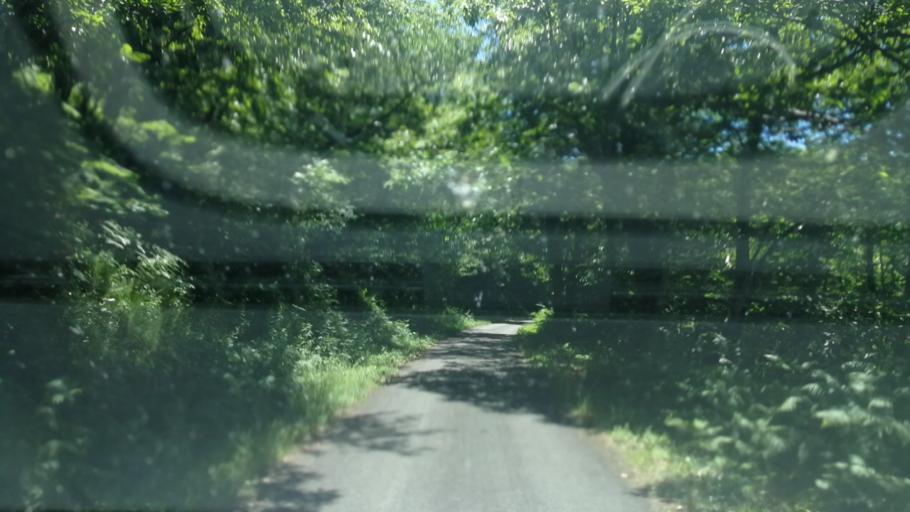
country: FR
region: Midi-Pyrenees
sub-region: Departement de l'Aveyron
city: Firmi
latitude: 44.5847
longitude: 2.3814
